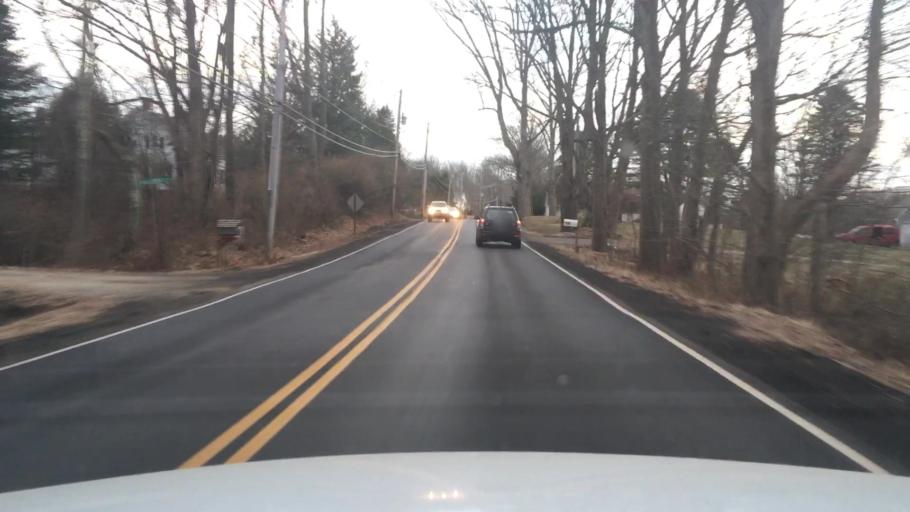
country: US
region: Maine
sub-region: Lincoln County
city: Damariscotta
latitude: 44.0087
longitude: -69.5311
